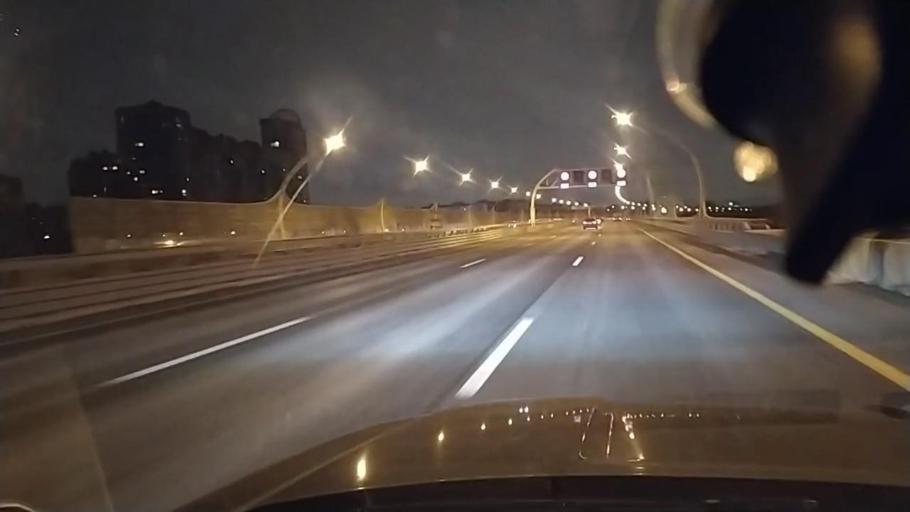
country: RU
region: Leningrad
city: Untolovo
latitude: 60.0238
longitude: 30.2132
